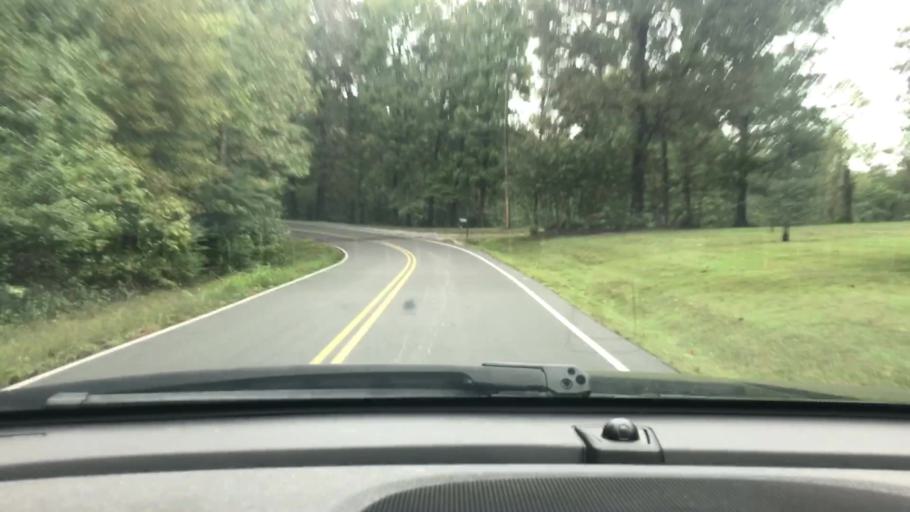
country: US
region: Tennessee
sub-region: Cheatham County
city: Kingston Springs
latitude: 36.1030
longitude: -87.1357
